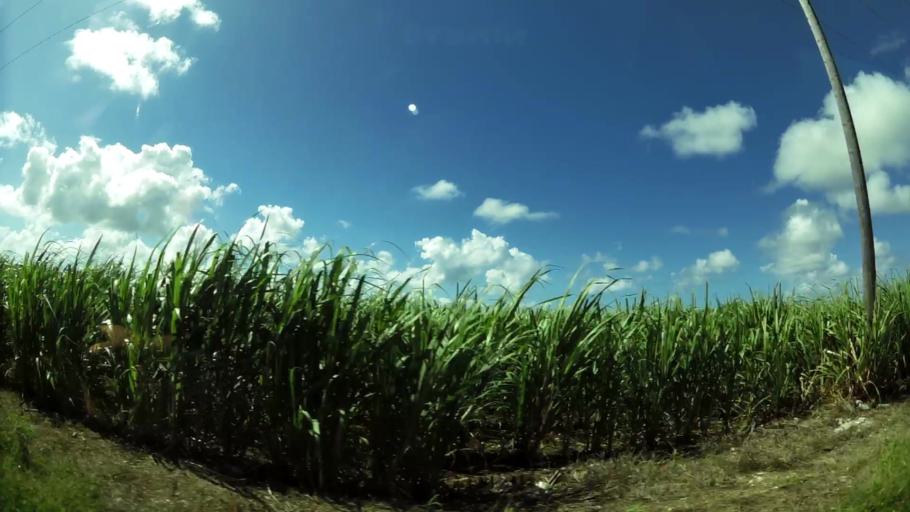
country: GP
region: Guadeloupe
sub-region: Guadeloupe
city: Petit-Canal
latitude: 16.4021
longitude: -61.4653
